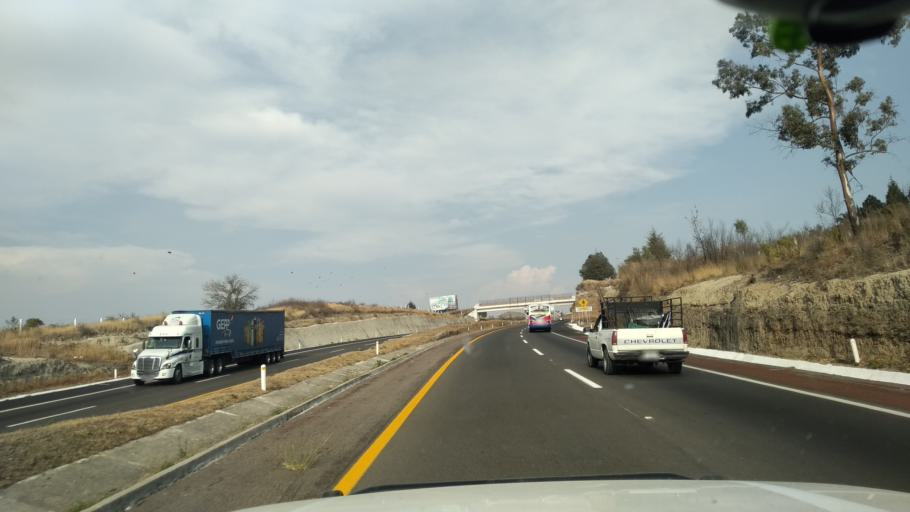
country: MX
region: Puebla
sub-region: Santa Isabel Cholula
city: San Pablo Ahuatempa
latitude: 18.9770
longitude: -98.3601
